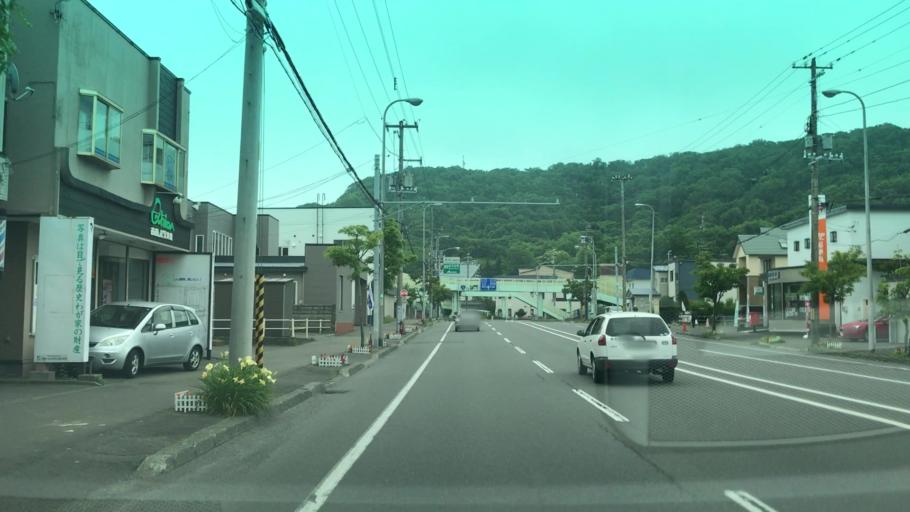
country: JP
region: Hokkaido
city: Muroran
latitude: 42.3561
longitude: 141.0471
